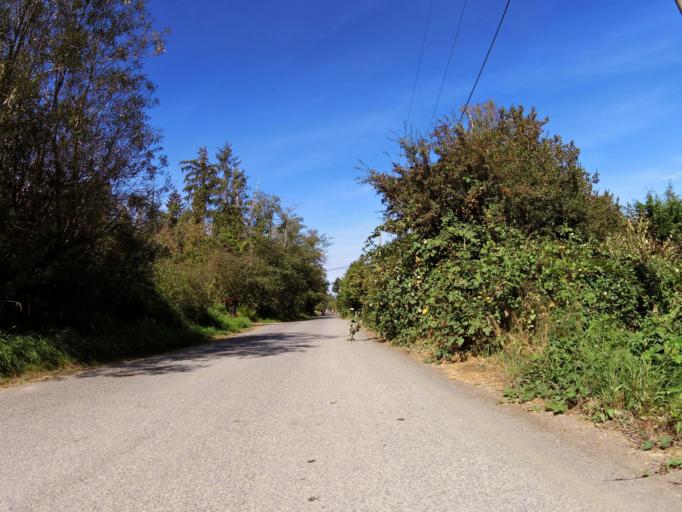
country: CA
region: British Columbia
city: North Saanich
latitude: 48.5585
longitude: -123.3874
